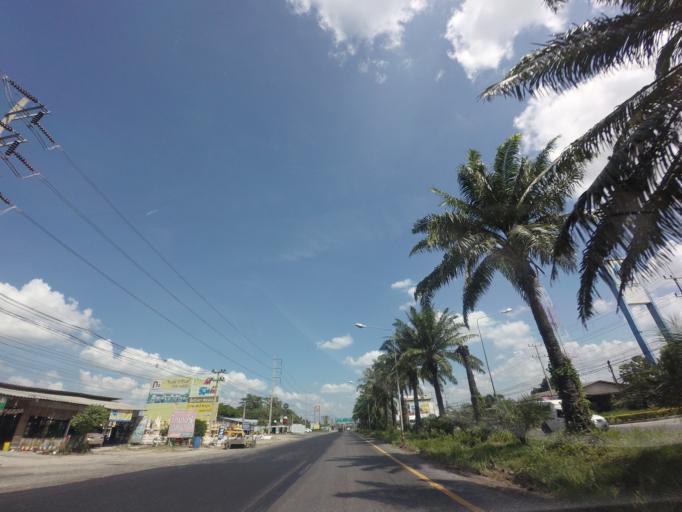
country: TH
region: Chon Buri
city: Ban Bueng
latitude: 13.3033
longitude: 101.1153
